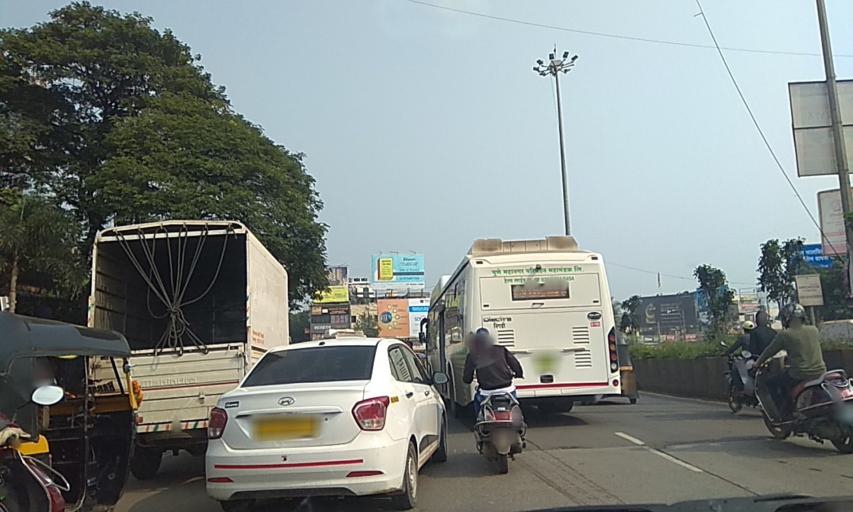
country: IN
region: Maharashtra
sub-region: Pune Division
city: Lohogaon
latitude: 18.5615
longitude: 73.9385
